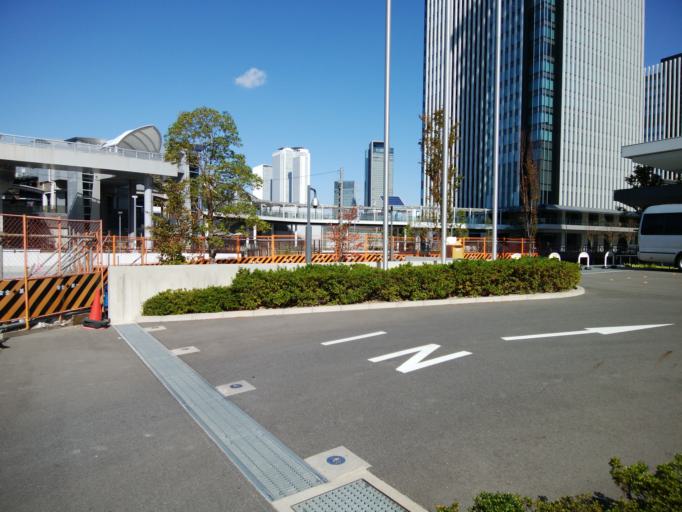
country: JP
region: Aichi
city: Nagoya-shi
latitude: 35.1608
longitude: 136.8820
